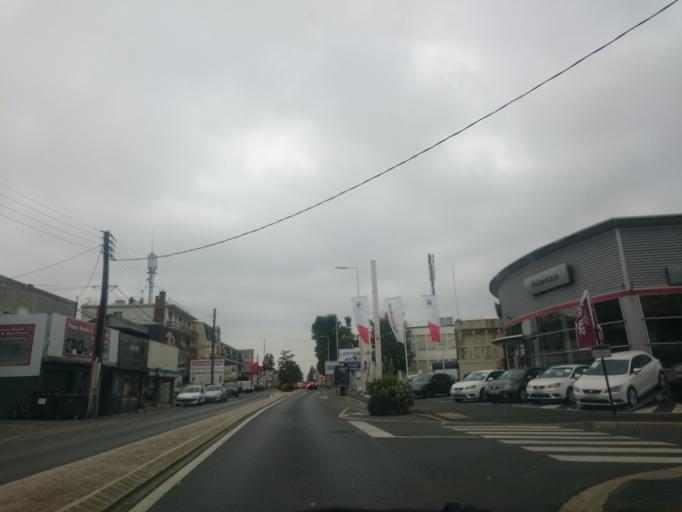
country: FR
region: Ile-de-France
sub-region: Departement de l'Essonne
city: Sainte-Genevieve-des-Bois
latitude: 48.6489
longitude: 2.3363
